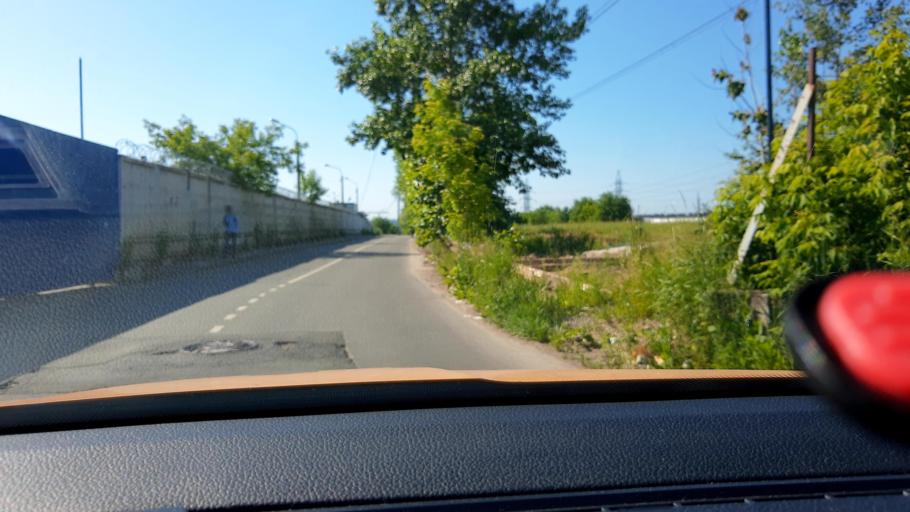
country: RU
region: Moskovskaya
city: Arkhangel'skoye
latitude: 55.7970
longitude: 37.3074
